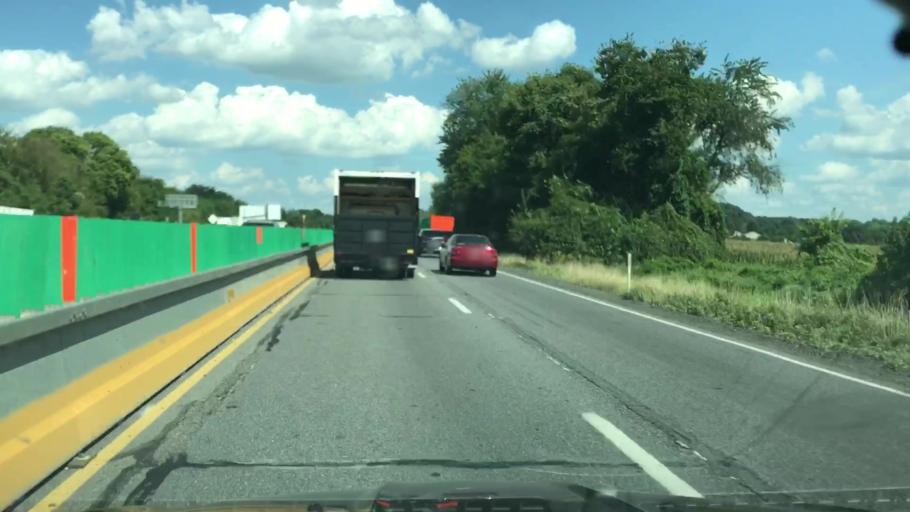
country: US
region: Pennsylvania
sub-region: Dauphin County
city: Highspire
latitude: 40.2243
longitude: -76.7763
